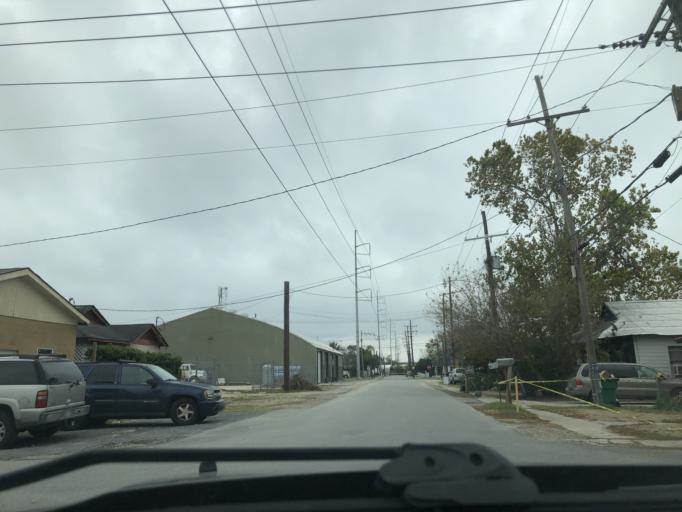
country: US
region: Louisiana
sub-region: Jefferson Parish
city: Metairie Terrace
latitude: 29.9727
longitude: -90.1620
